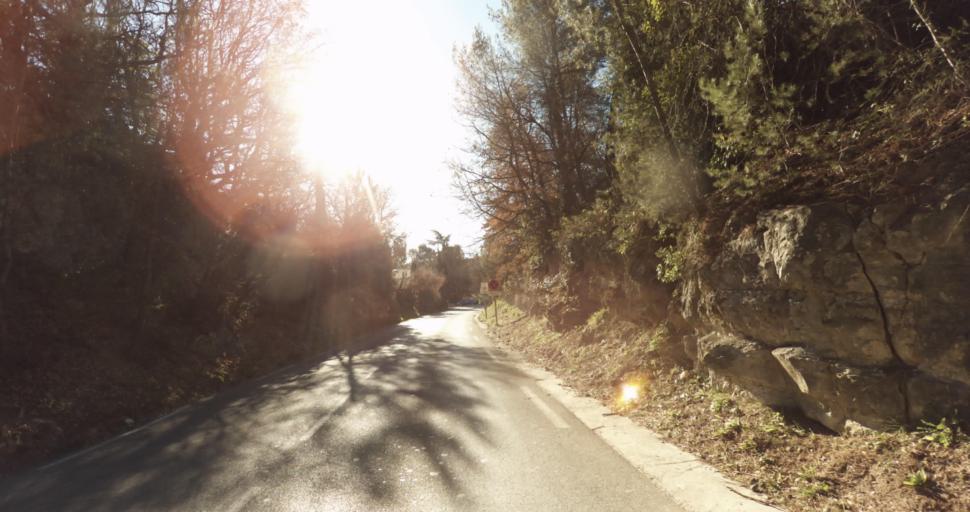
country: FR
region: Provence-Alpes-Cote d'Azur
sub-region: Departement des Bouches-du-Rhone
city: Cadolive
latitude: 43.3947
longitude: 5.5513
